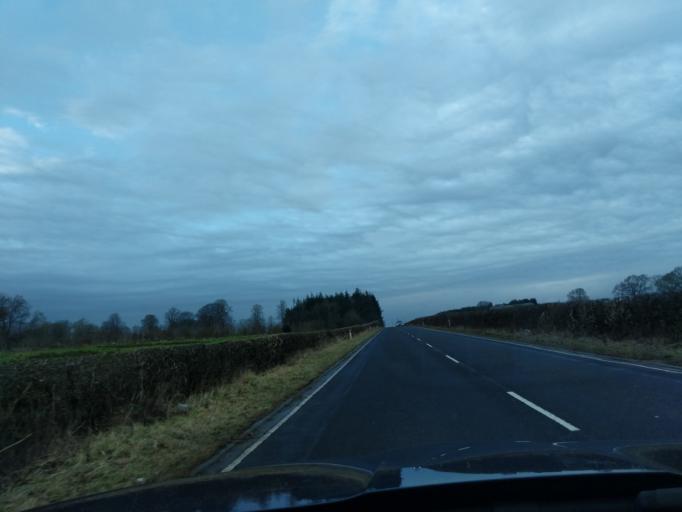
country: GB
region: England
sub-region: Northumberland
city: Rothley
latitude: 55.1245
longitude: -1.9270
